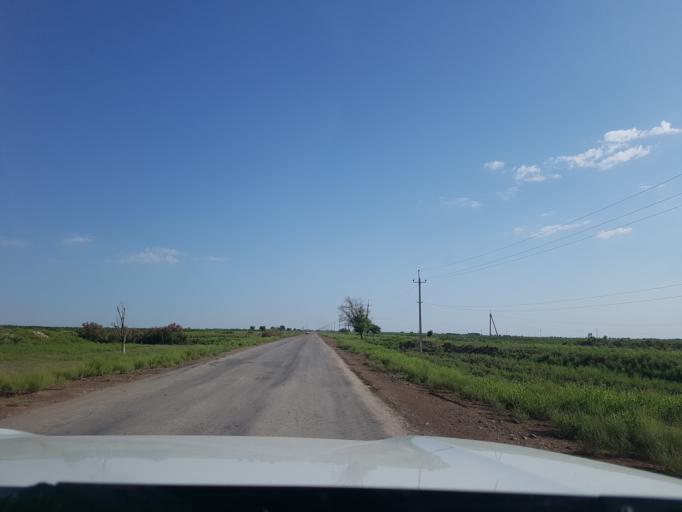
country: TM
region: Dasoguz
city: Koeneuergench
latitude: 41.8631
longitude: 58.7055
